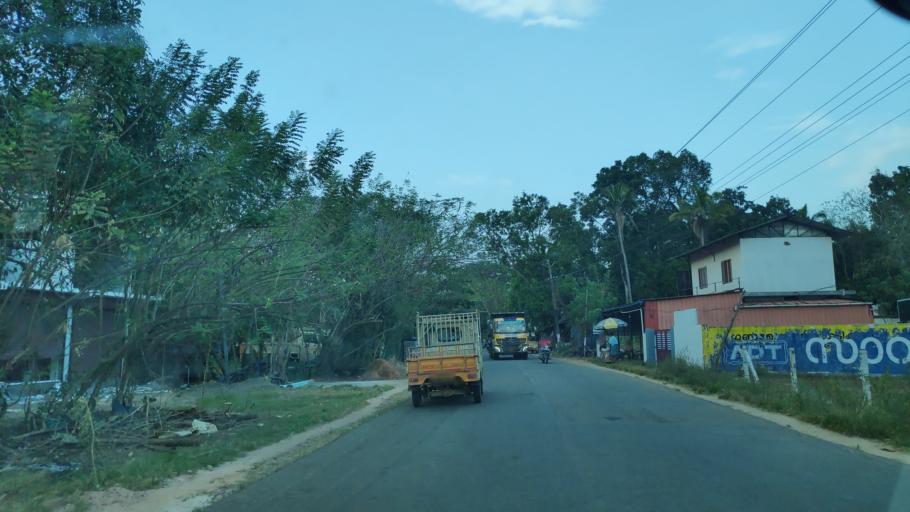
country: IN
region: Kerala
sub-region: Alappuzha
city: Shertallai
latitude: 9.6390
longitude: 76.3716
